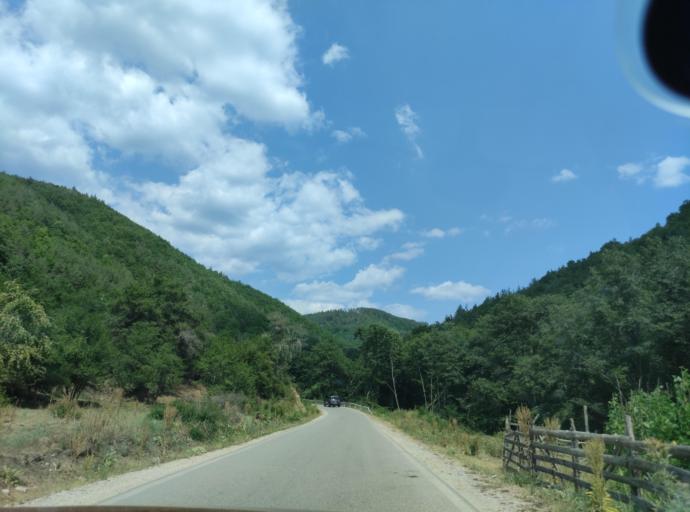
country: BG
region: Blagoevgrad
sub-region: Obshtina Belitsa
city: Belitsa
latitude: 42.0021
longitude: 23.5507
